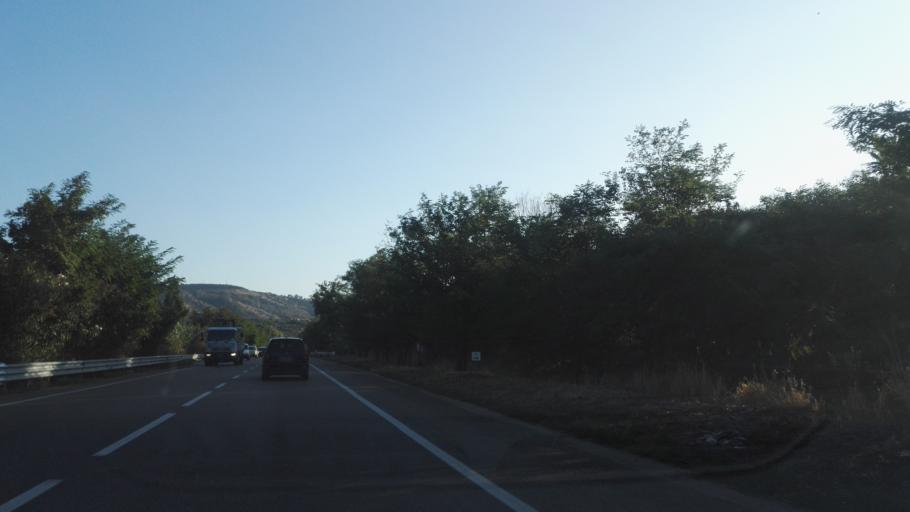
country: IT
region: Calabria
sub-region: Provincia di Catanzaro
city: Montepaone Lido
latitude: 38.7225
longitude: 16.5344
